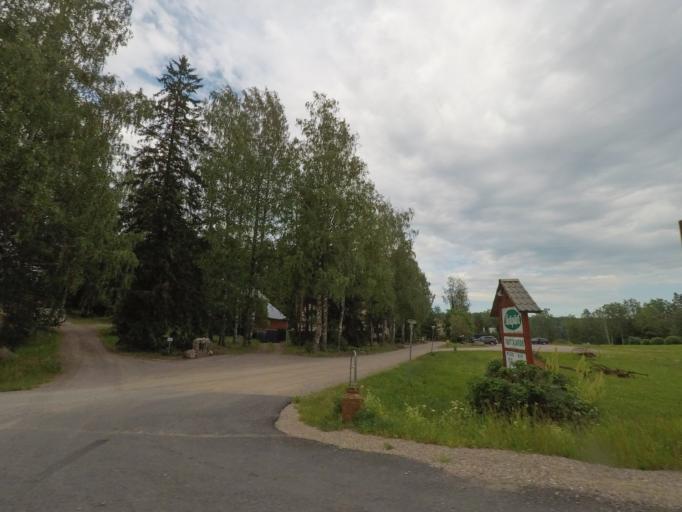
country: FI
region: Uusimaa
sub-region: Helsinki
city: Maentsaelae
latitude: 60.7478
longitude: 25.4322
